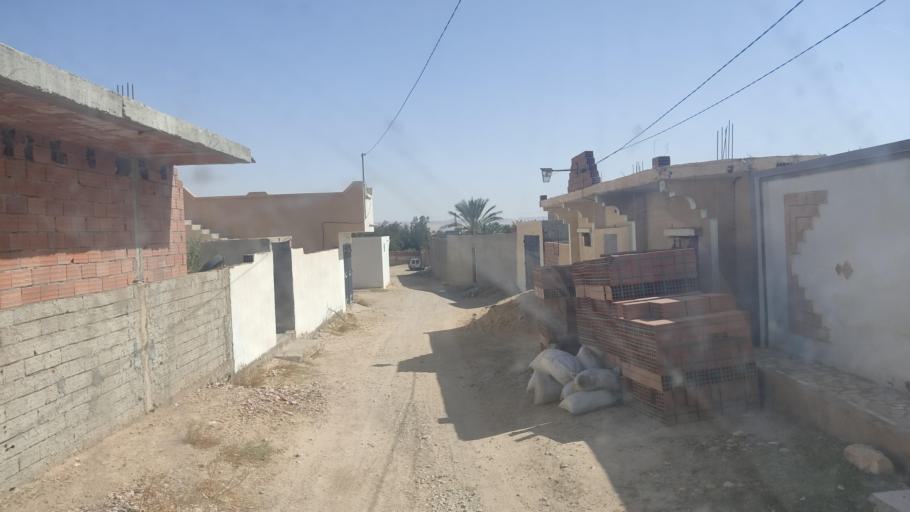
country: TN
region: Gafsa
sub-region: Gafsa Municipality
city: Gafsa
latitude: 34.3384
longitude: 8.9215
